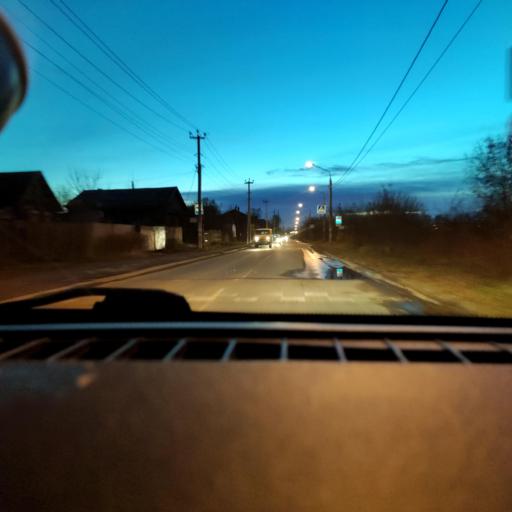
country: RU
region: Perm
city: Perm
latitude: 58.0268
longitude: 56.2039
